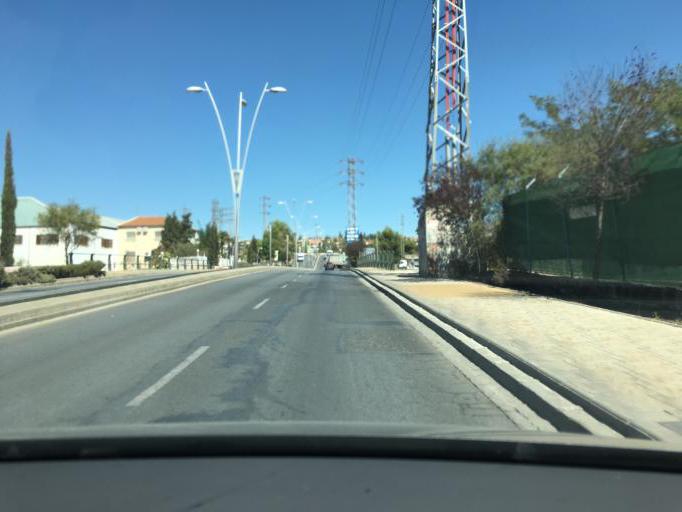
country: ES
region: Andalusia
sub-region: Provincia de Granada
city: Albolote
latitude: 37.2345
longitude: -3.6484
